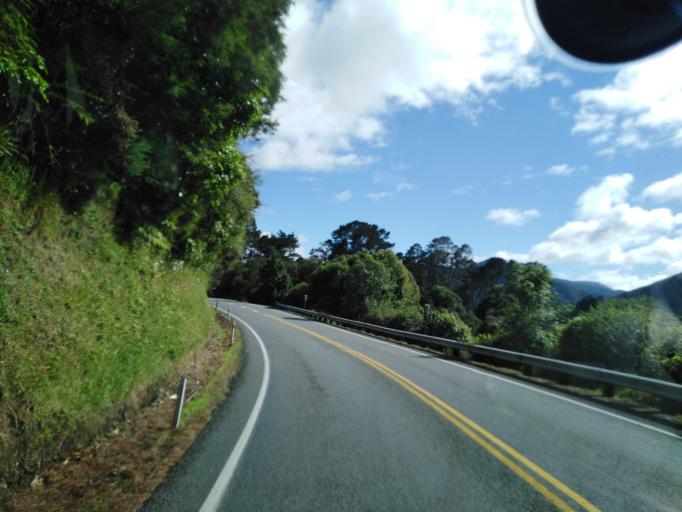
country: NZ
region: Nelson
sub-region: Nelson City
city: Nelson
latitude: -41.2869
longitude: 173.5720
